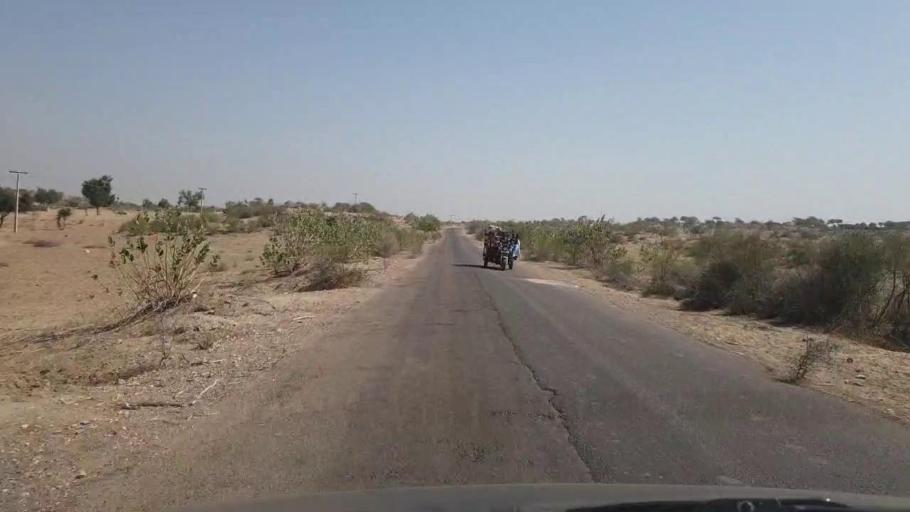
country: PK
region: Sindh
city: Chor
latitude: 25.5926
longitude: 69.9501
